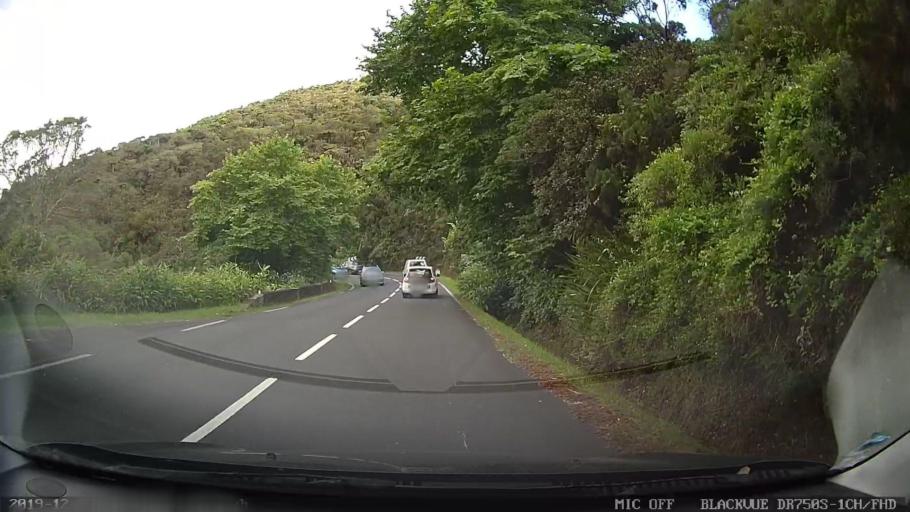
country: RE
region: Reunion
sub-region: Reunion
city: Cilaos
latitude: -21.1615
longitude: 55.5946
